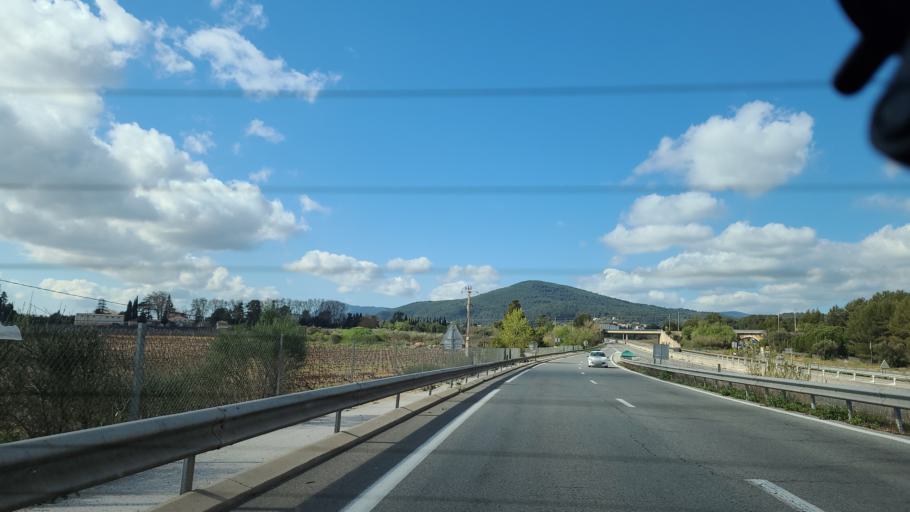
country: FR
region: Provence-Alpes-Cote d'Azur
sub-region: Departement du Var
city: Cuers
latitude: 43.2469
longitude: 6.0930
